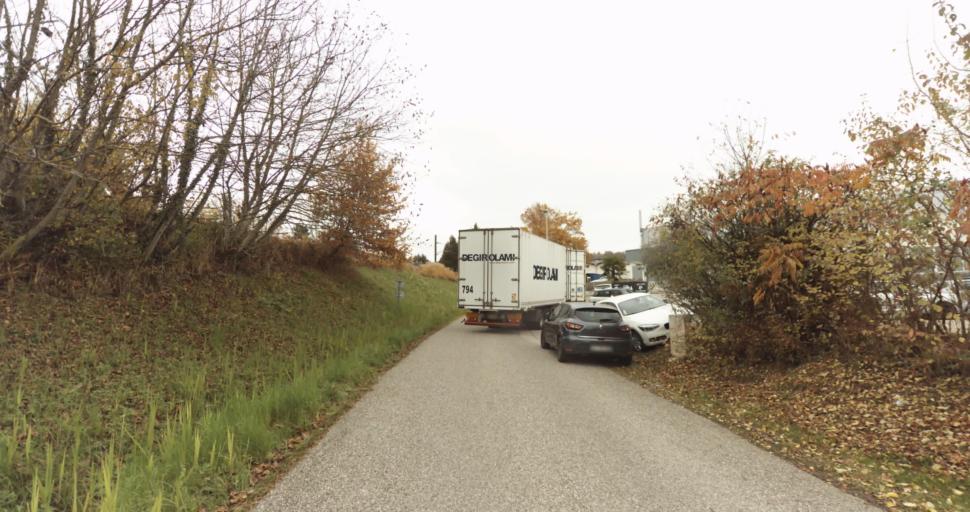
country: FR
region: Rhone-Alpes
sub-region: Departement de la Haute-Savoie
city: Pringy
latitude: 45.9435
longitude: 6.1247
